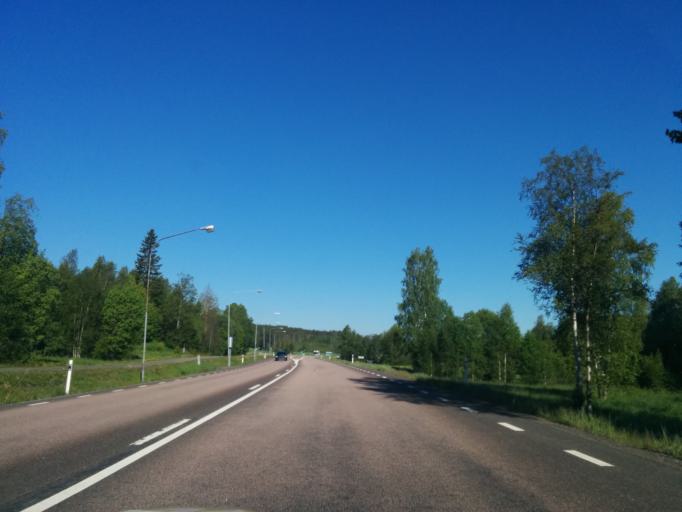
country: SE
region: Vaesternorrland
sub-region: Haernoesands Kommun
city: Haernoesand
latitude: 62.6653
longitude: 17.8494
